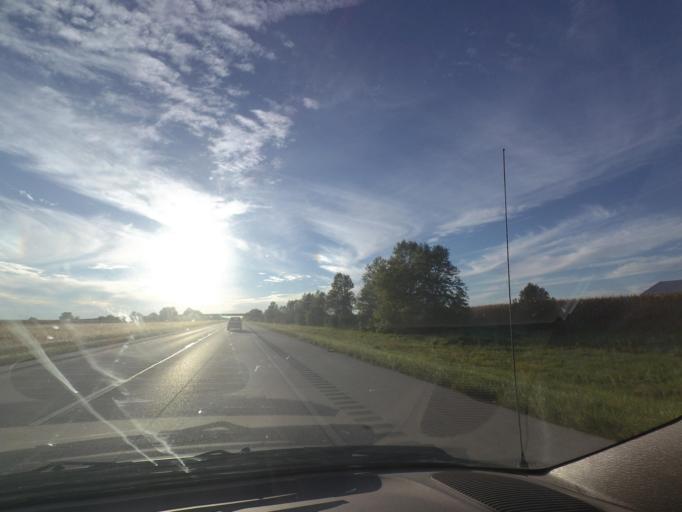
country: US
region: Illinois
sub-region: Sangamon County
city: New Berlin
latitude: 39.7413
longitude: -89.8401
